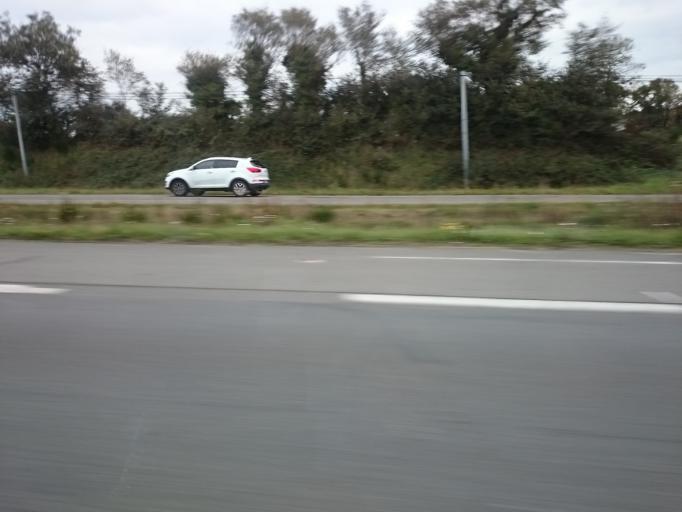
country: FR
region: Brittany
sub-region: Departement du Morbihan
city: Muzillac
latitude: 47.5671
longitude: -2.5139
